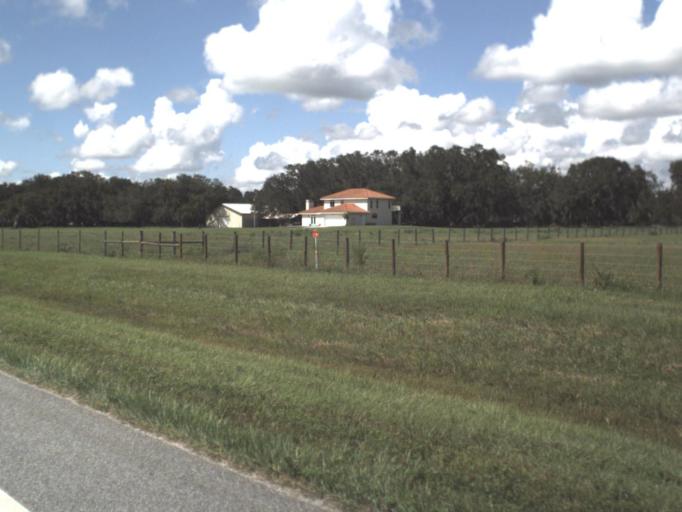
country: US
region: Florida
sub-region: Sarasota County
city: Lake Sarasota
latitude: 27.3406
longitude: -82.1489
